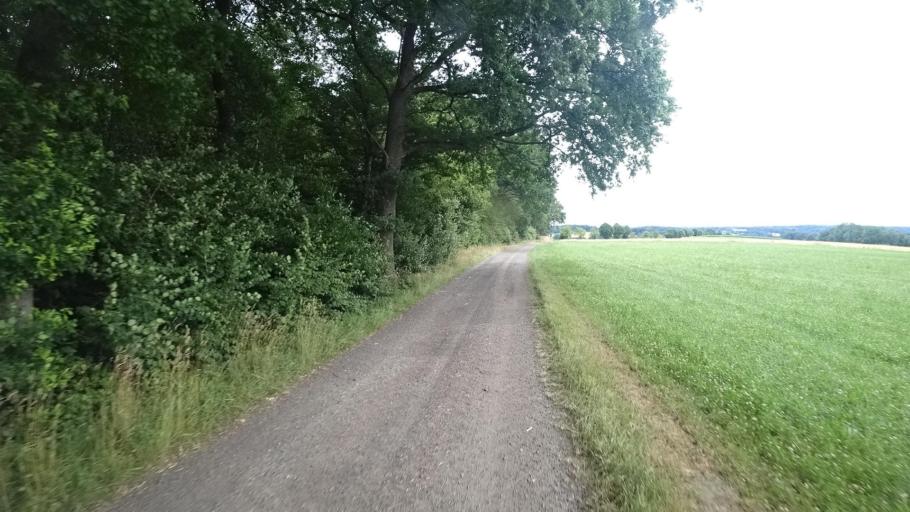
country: DE
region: Rheinland-Pfalz
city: Orfgen
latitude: 50.6742
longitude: 7.5388
